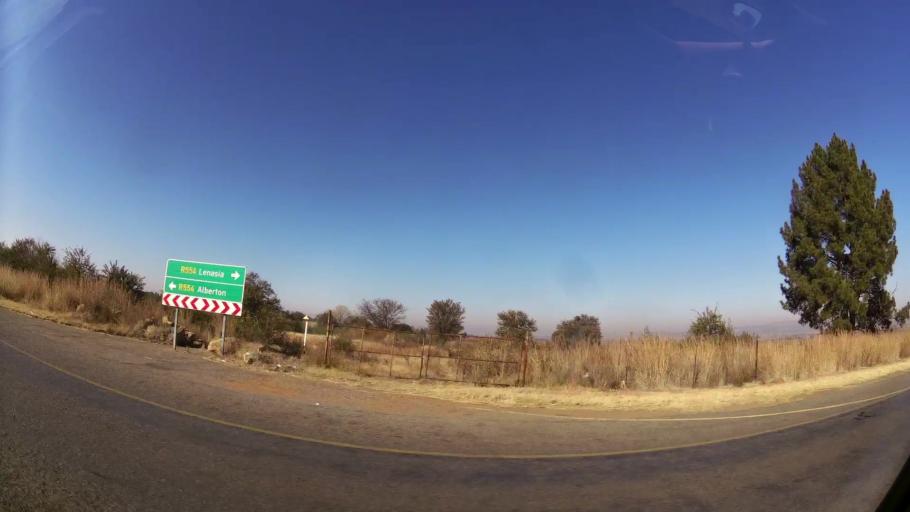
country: ZA
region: Gauteng
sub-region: City of Johannesburg Metropolitan Municipality
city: Johannesburg
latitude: -26.3127
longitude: 28.0797
